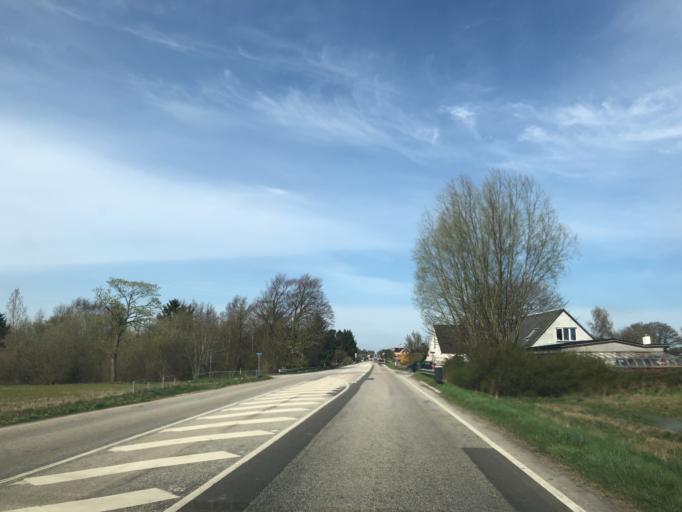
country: DK
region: Zealand
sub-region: Faxe Kommune
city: Ronnede
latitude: 55.3011
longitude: 12.0451
